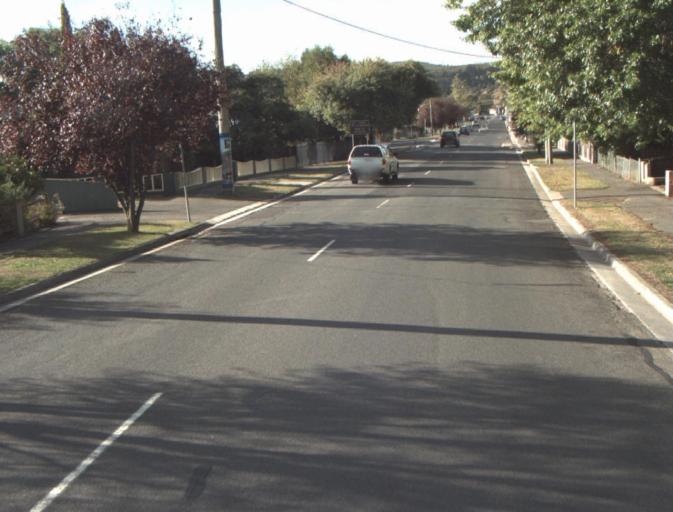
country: AU
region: Tasmania
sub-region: Launceston
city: Mayfield
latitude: -41.2534
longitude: 147.2157
